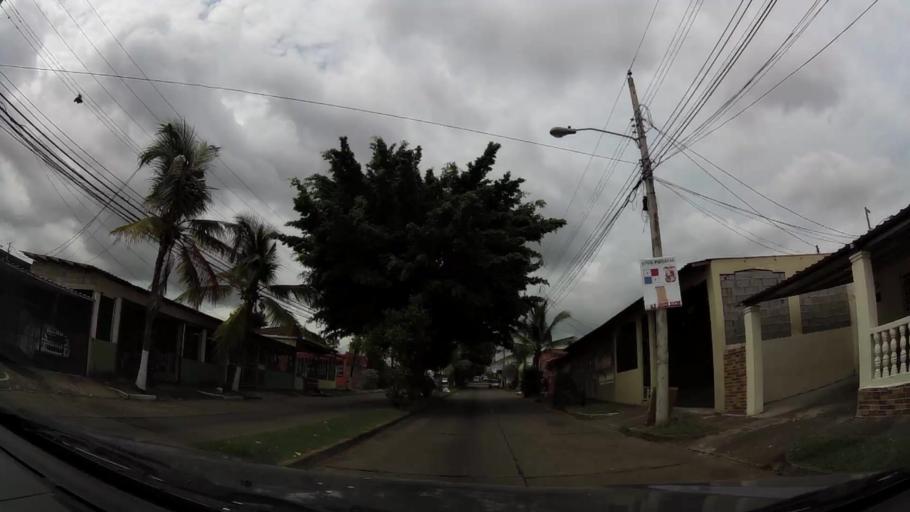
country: PA
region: Panama
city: San Miguelito
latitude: 9.0516
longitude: -79.4212
